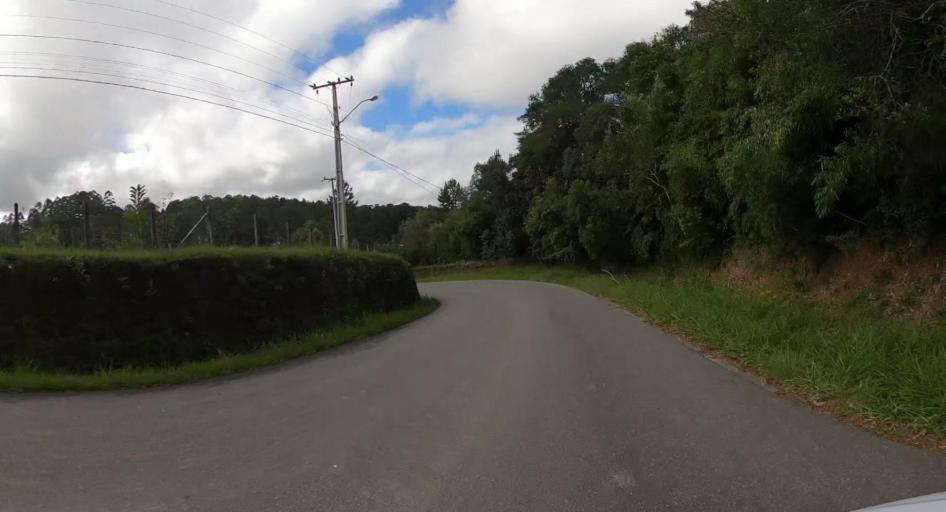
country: BR
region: Parana
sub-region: Campina Grande Do Sul
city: Campina Grande do Sul
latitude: -25.2991
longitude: -49.0431
